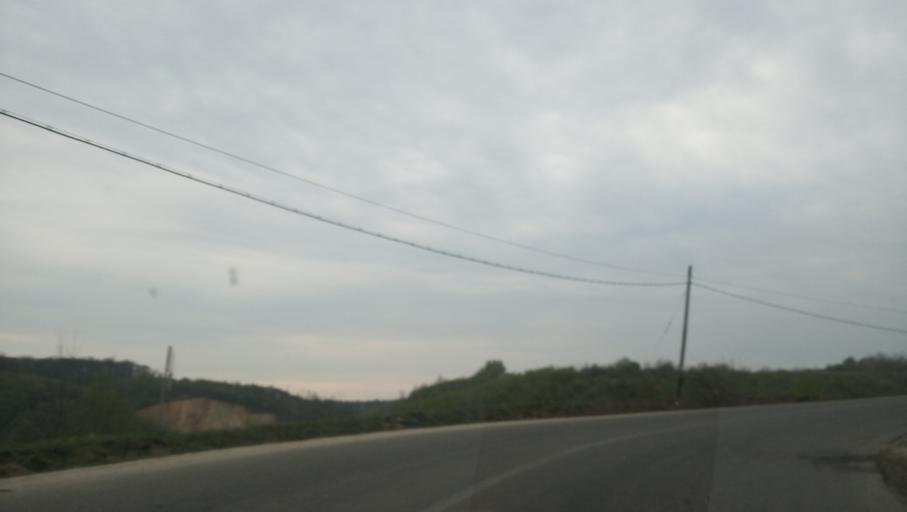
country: RO
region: Bihor
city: Hidiselu de Sus
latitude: 46.9257
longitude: 22.0543
